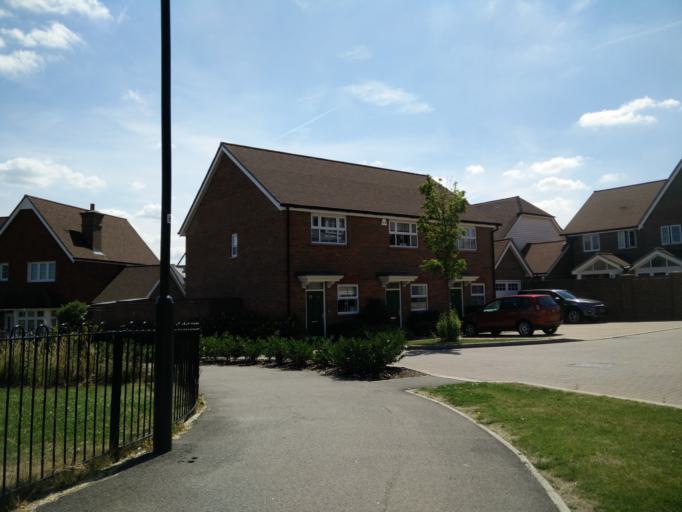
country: GB
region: England
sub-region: West Sussex
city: Horsham
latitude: 51.0638
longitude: -0.3540
